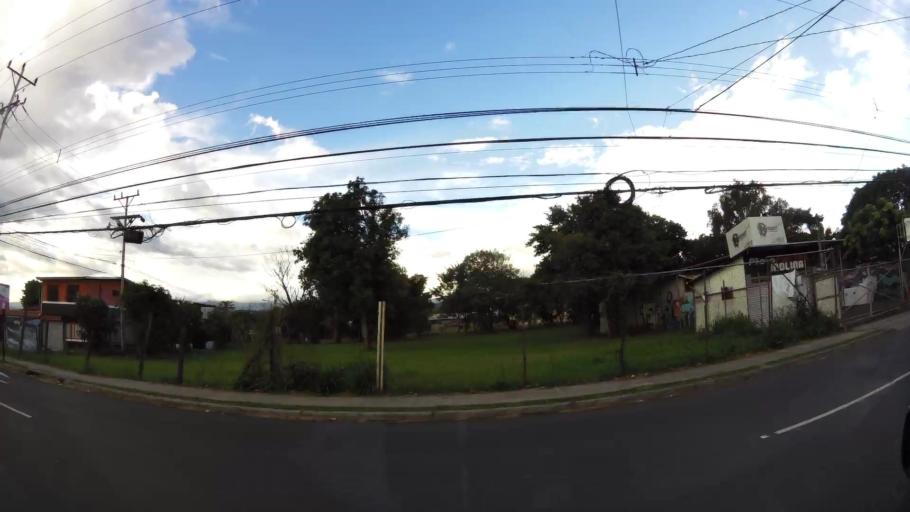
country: CR
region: Alajuela
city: Alajuela
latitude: 10.0008
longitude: -84.1981
